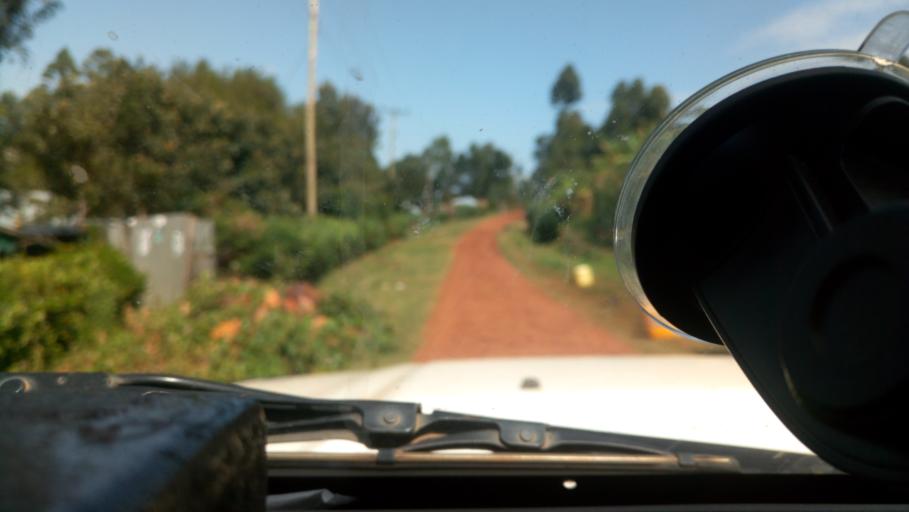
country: KE
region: Kisii
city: Ogembo
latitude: -0.9124
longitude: 34.8174
